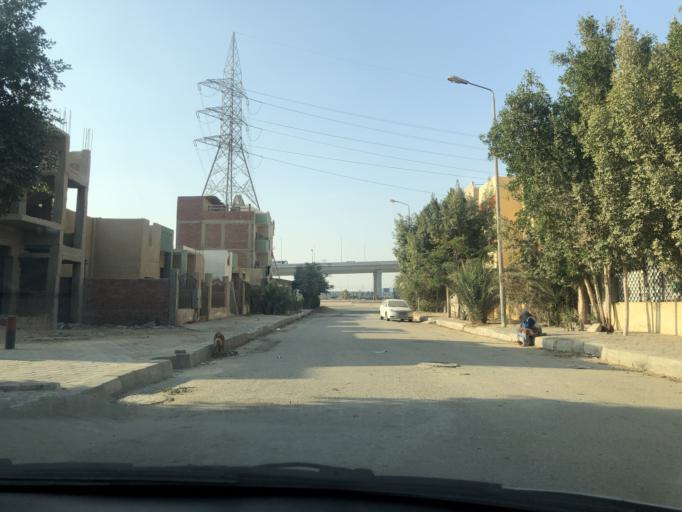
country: EG
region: Al Jizah
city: Madinat Sittah Uktubar
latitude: 29.9084
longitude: 30.9306
